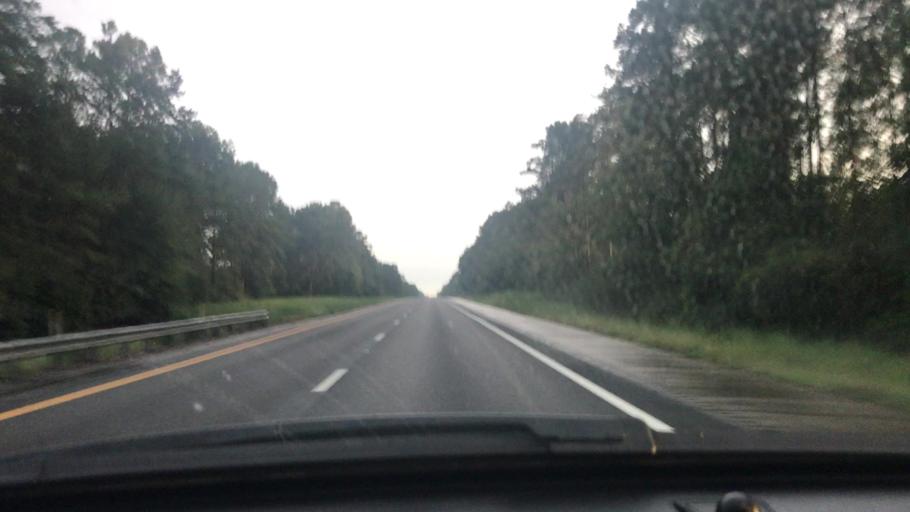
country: US
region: Mississippi
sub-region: Pike County
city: Magnolia
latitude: 31.0905
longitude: -90.4892
